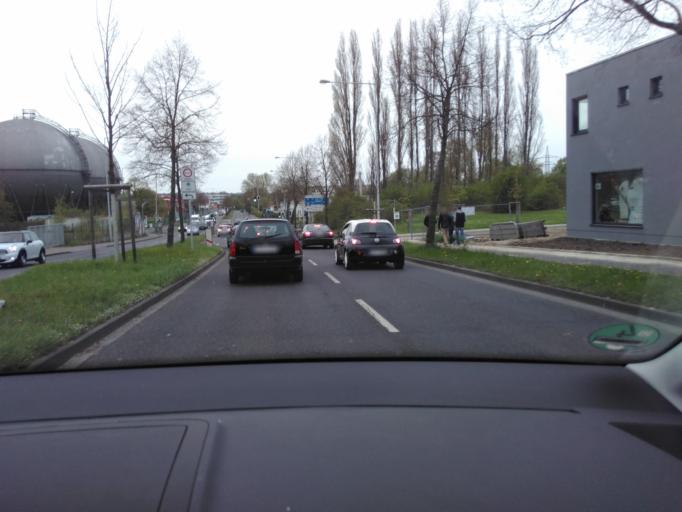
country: DE
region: North Rhine-Westphalia
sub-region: Regierungsbezirk Koln
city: Wurselen
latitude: 50.7946
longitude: 6.1137
